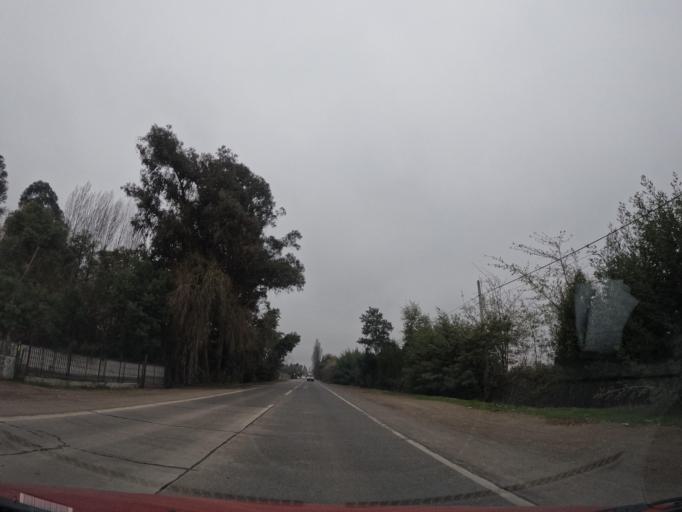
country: CL
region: Maule
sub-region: Provincia de Talca
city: San Clemente
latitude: -35.5658
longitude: -71.4473
